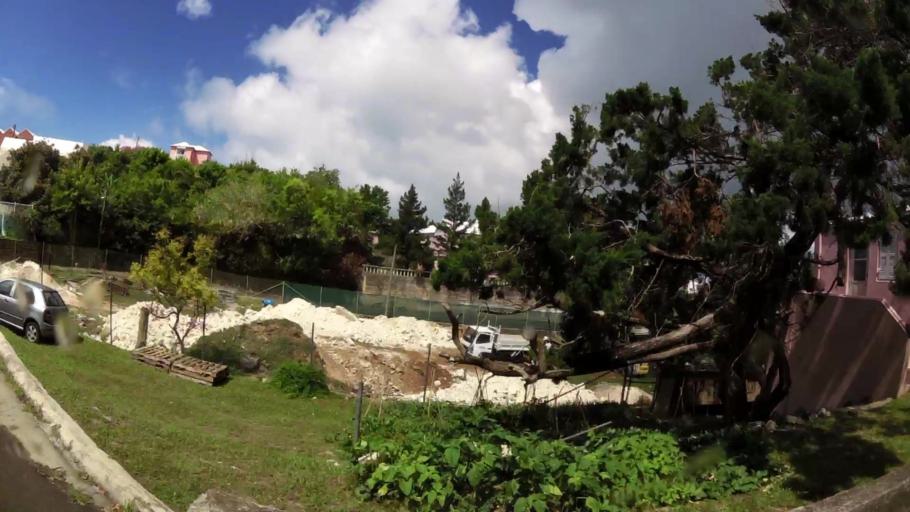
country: BM
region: Saint George
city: Saint George
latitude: 32.3664
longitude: -64.6550
